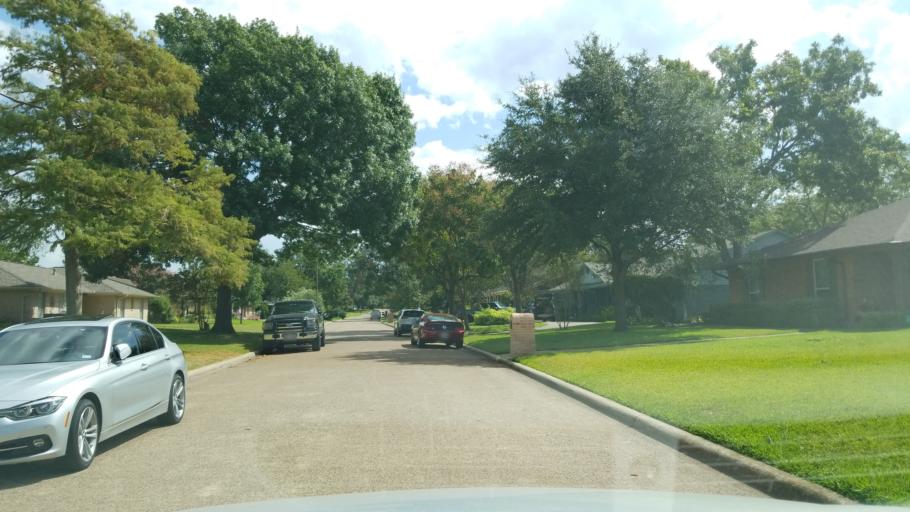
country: US
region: Texas
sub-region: Dallas County
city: Richardson
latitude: 32.9540
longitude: -96.7776
